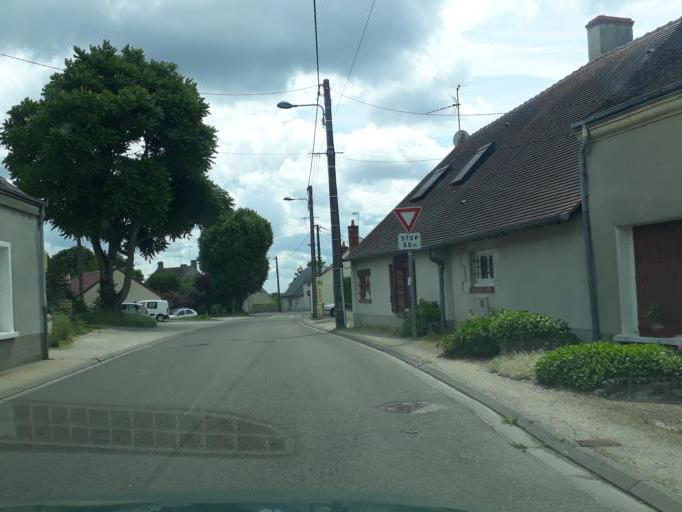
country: FR
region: Centre
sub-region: Departement du Loiret
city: Ingre
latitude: 47.9239
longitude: 1.8200
